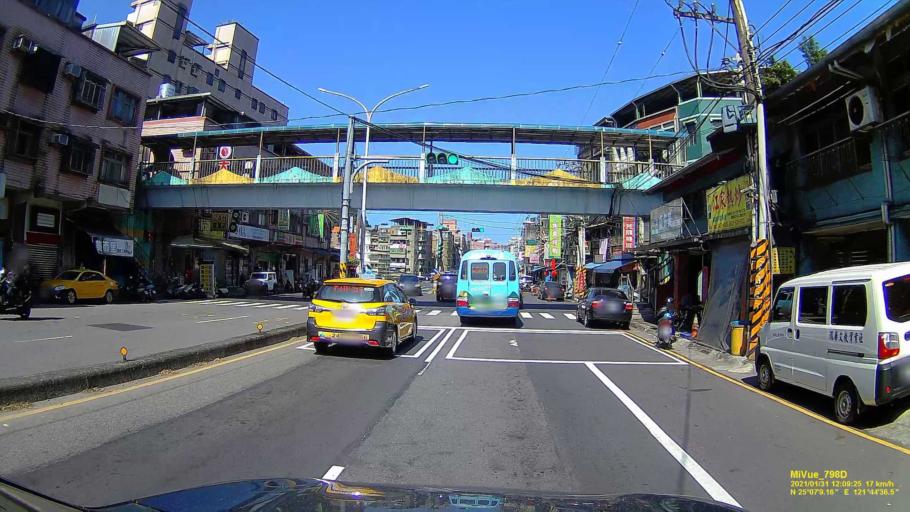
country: TW
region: Taiwan
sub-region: Keelung
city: Keelung
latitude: 25.1193
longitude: 121.7434
